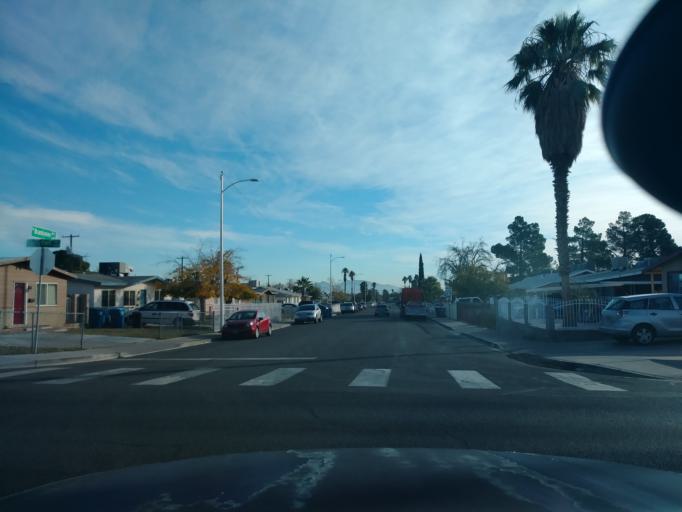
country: US
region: Nevada
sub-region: Clark County
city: Spring Valley
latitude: 36.1650
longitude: -115.2331
